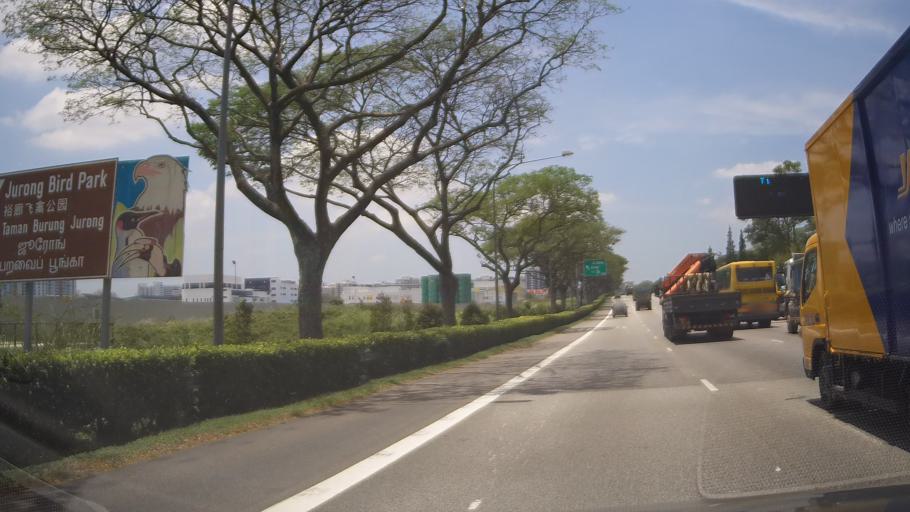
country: MY
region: Johor
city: Johor Bahru
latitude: 1.3599
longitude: 103.7024
